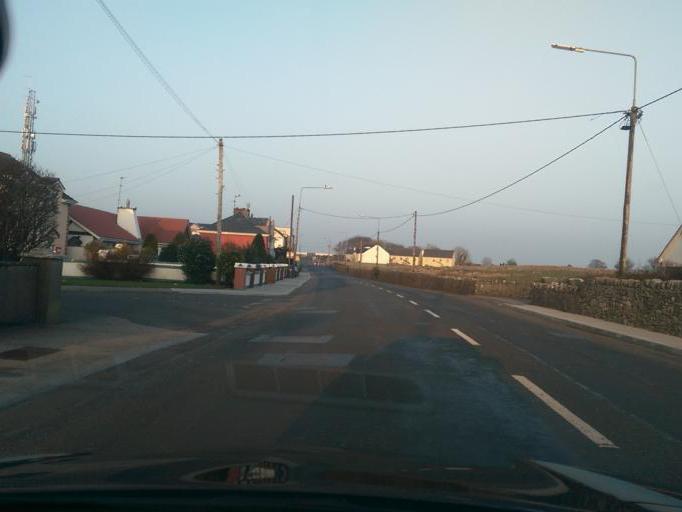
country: IE
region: Connaught
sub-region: County Galway
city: Loughrea
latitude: 53.2012
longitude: -8.5557
